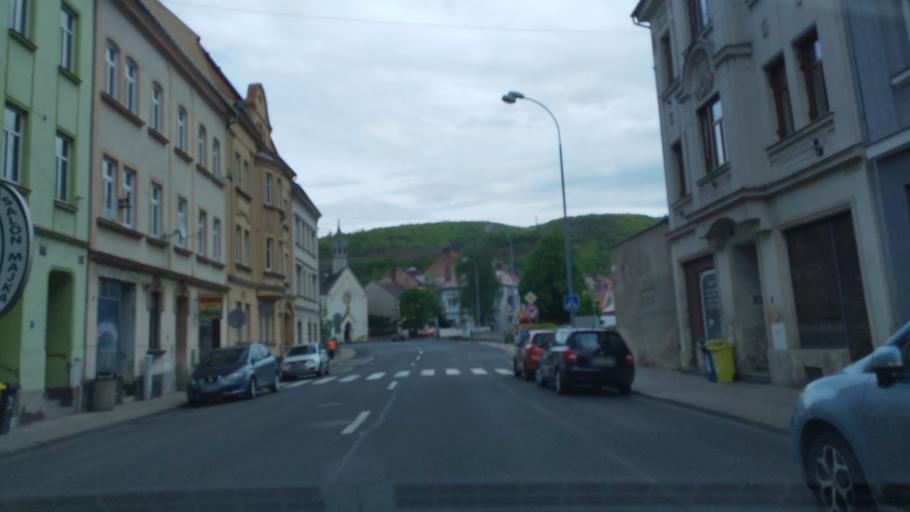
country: CZ
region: Ustecky
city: Trmice
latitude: 50.6424
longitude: 14.0002
